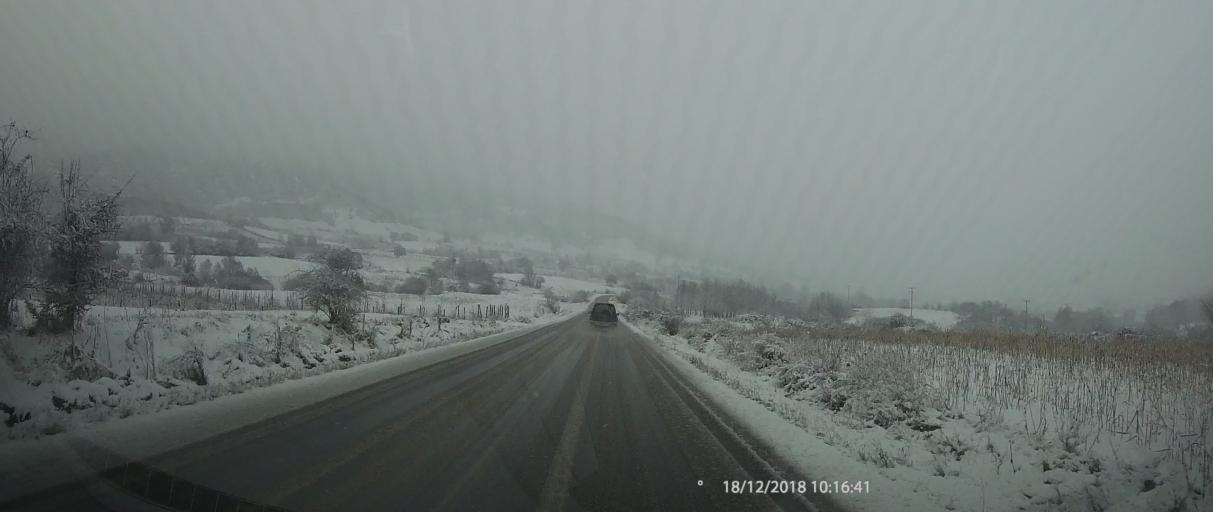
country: GR
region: Thessaly
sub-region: Nomos Larisis
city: Livadi
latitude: 40.1180
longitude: 22.2106
